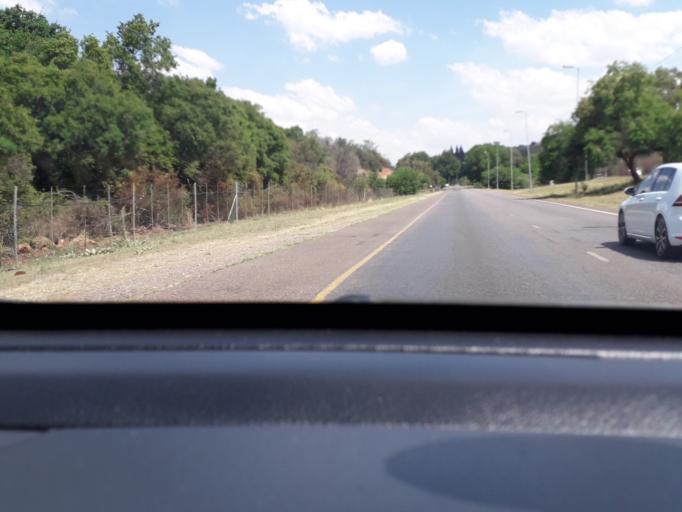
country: ZA
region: Gauteng
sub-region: City of Tshwane Metropolitan Municipality
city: Pretoria
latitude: -25.7923
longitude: 28.1965
